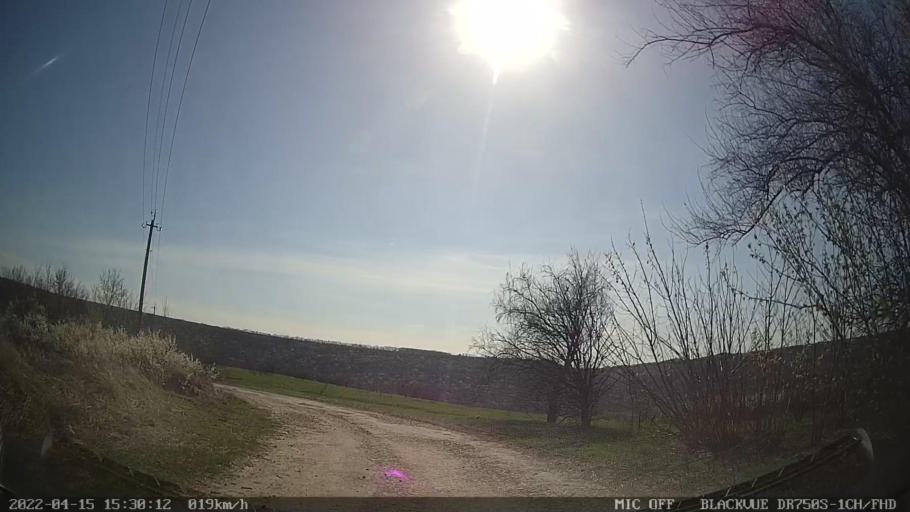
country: MD
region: Raionul Ocnita
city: Otaci
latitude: 48.3554
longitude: 27.9226
